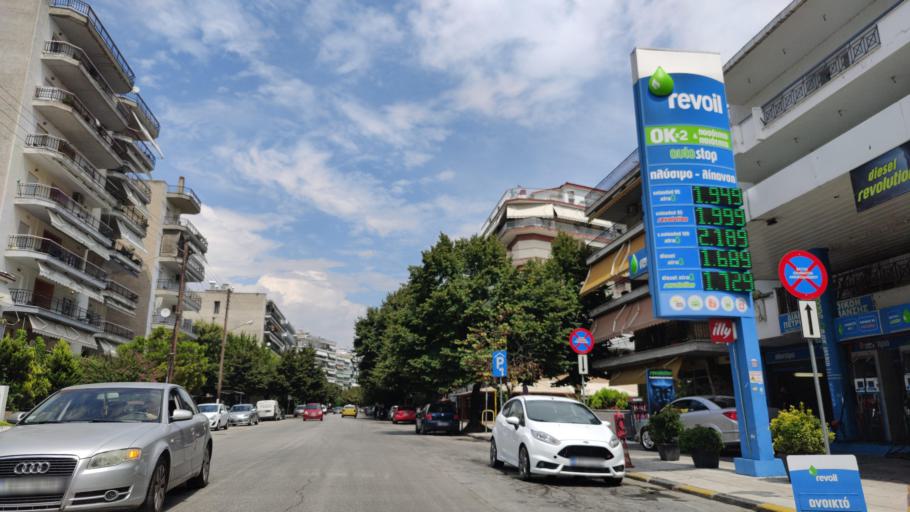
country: GR
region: Central Macedonia
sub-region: Nomos Serron
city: Serres
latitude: 41.0838
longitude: 23.5438
